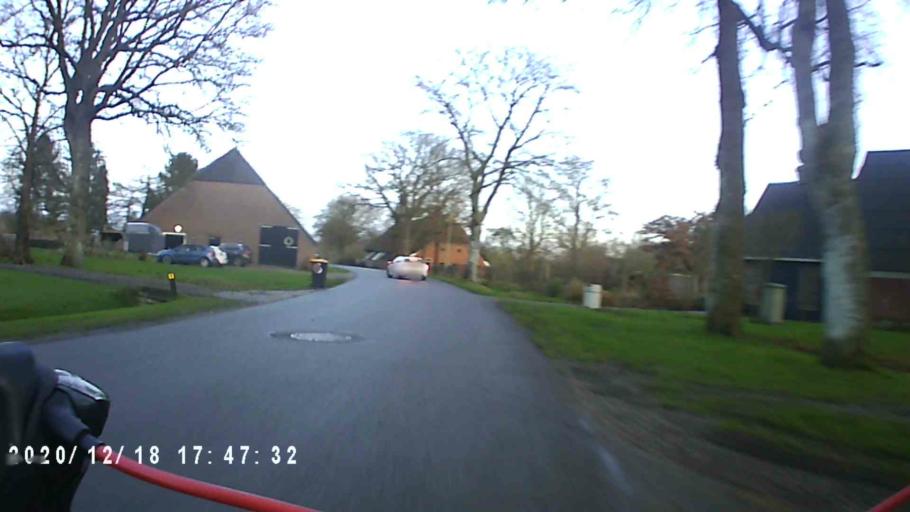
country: NL
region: Drenthe
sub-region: Gemeente Tynaarlo
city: Vries
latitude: 53.1112
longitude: 6.5790
